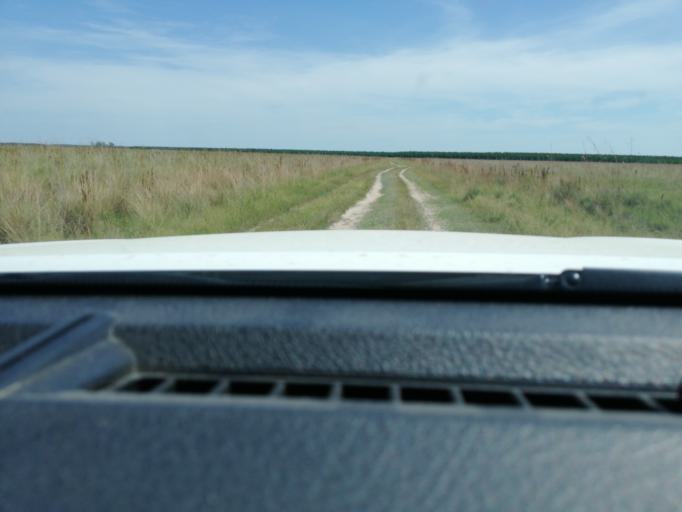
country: AR
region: Corrientes
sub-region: Departamento de San Miguel
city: San Miguel
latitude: -28.0497
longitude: -57.4556
